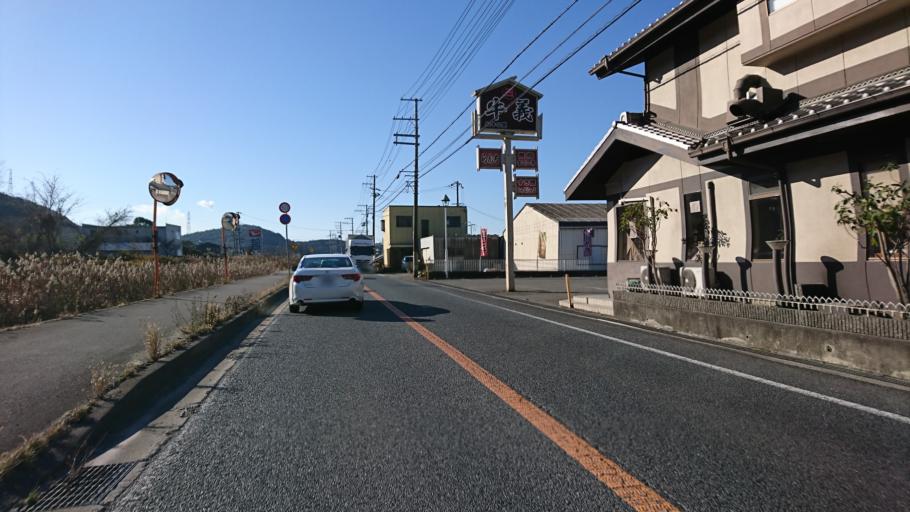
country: JP
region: Hyogo
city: Kakogawacho-honmachi
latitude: 34.8104
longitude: 134.8361
